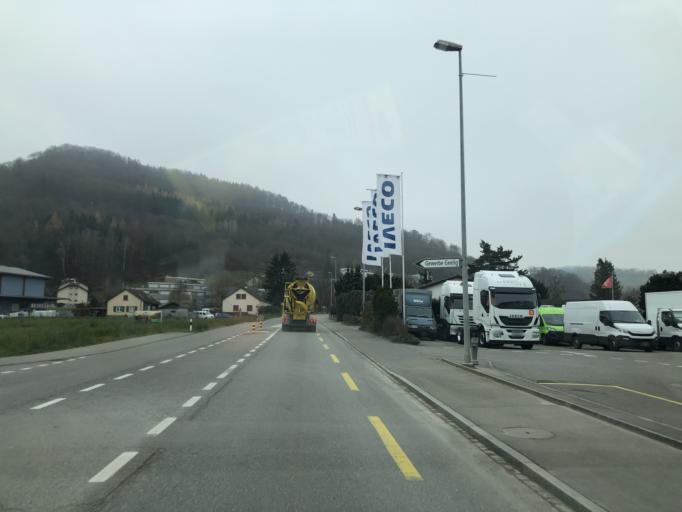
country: CH
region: Aargau
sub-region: Bezirk Baden
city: Gebenstorf
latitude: 47.4893
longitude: 8.2414
